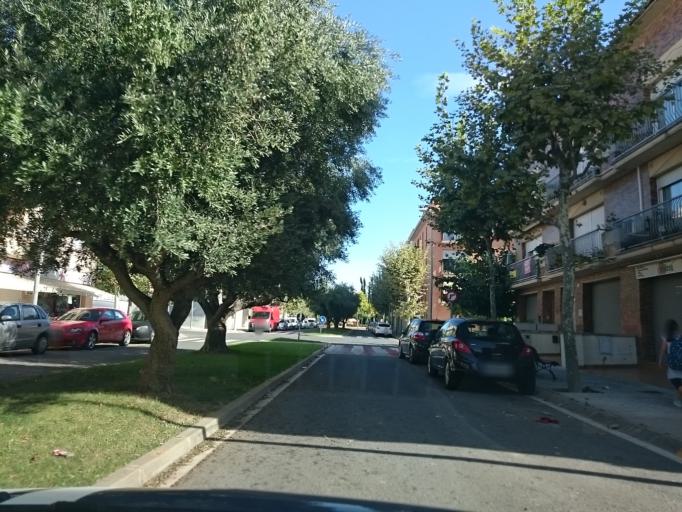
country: ES
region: Catalonia
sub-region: Provincia de Barcelona
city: Castellet
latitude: 41.2657
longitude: 1.5972
